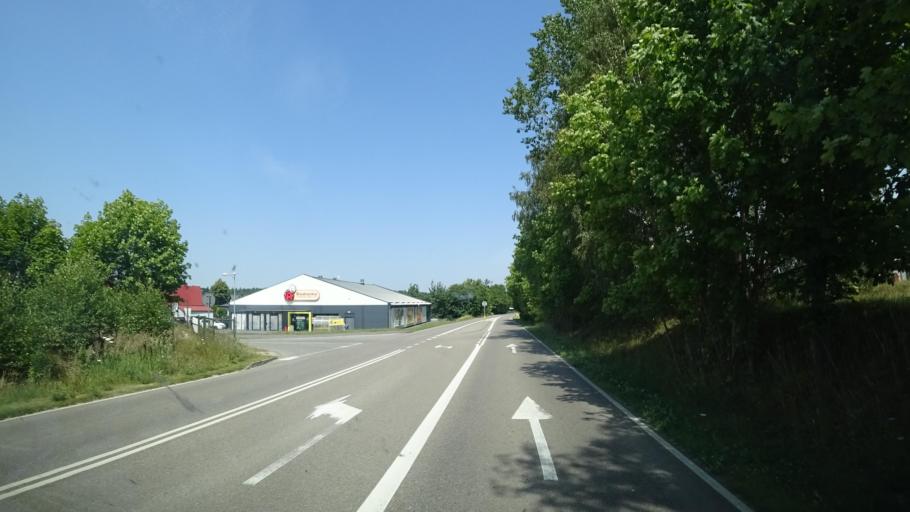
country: PL
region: Pomeranian Voivodeship
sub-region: Powiat koscierski
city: Dziemiany
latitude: 54.0077
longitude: 17.7729
